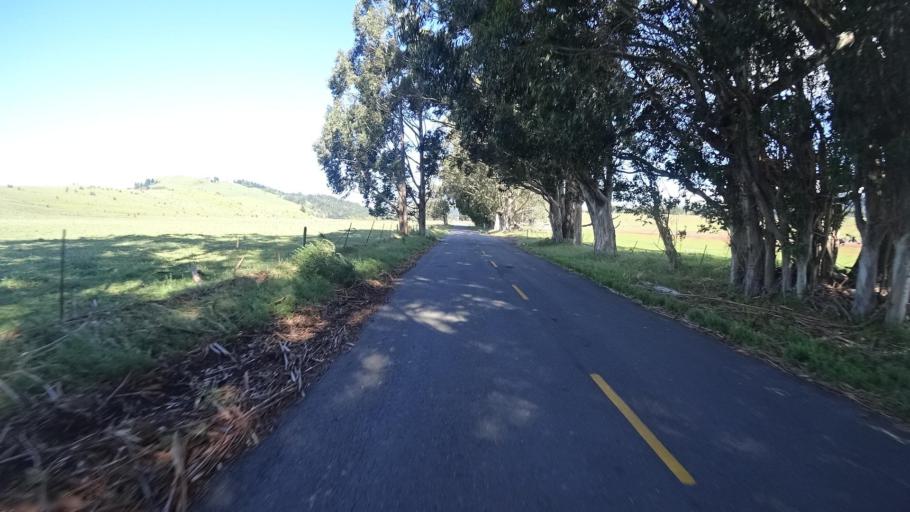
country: US
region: California
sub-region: Humboldt County
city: Ferndale
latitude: 40.3358
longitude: -124.3081
